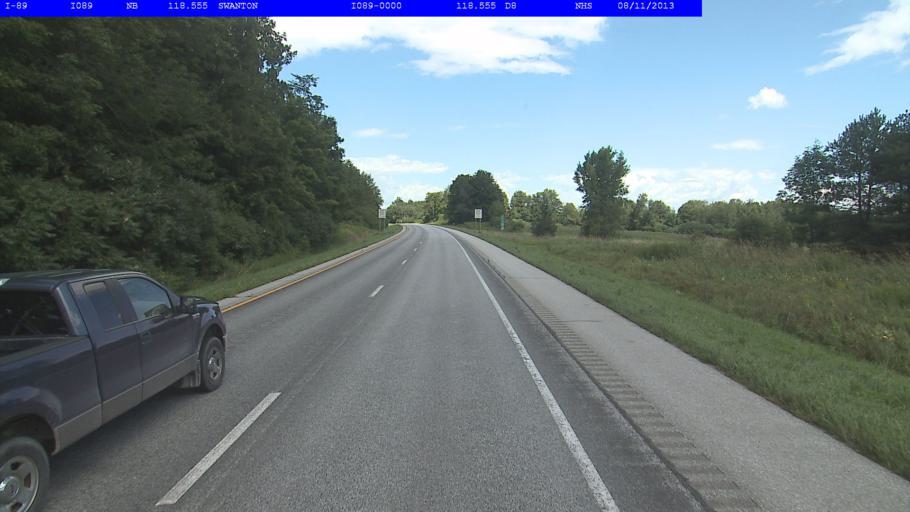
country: US
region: Vermont
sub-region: Franklin County
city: Saint Albans
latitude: 44.8565
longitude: -73.0808
